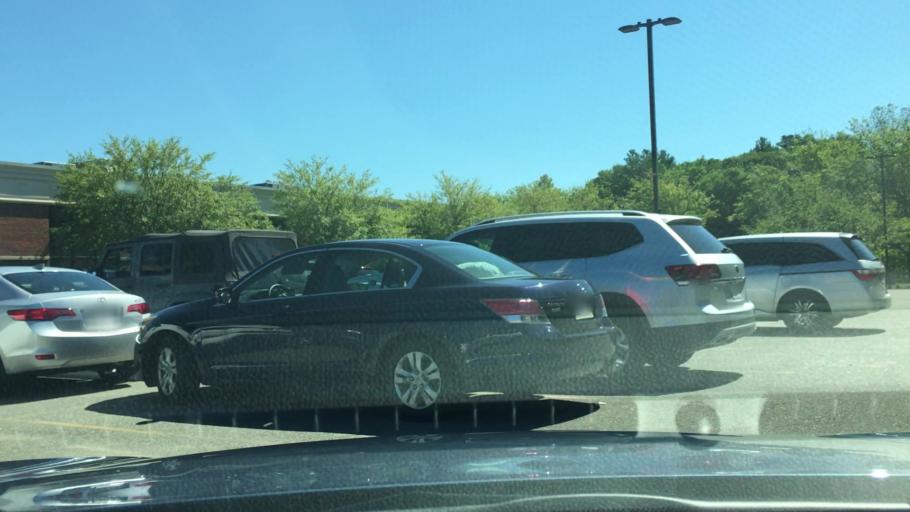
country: US
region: Massachusetts
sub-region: Middlesex County
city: Pinehurst
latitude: 42.5007
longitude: -71.2360
